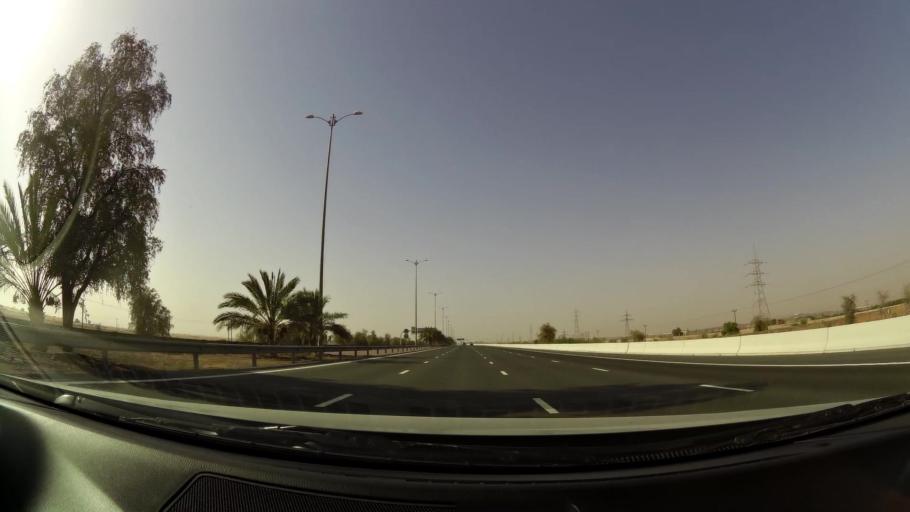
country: OM
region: Al Buraimi
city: Al Buraymi
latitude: 24.5093
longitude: 55.7655
